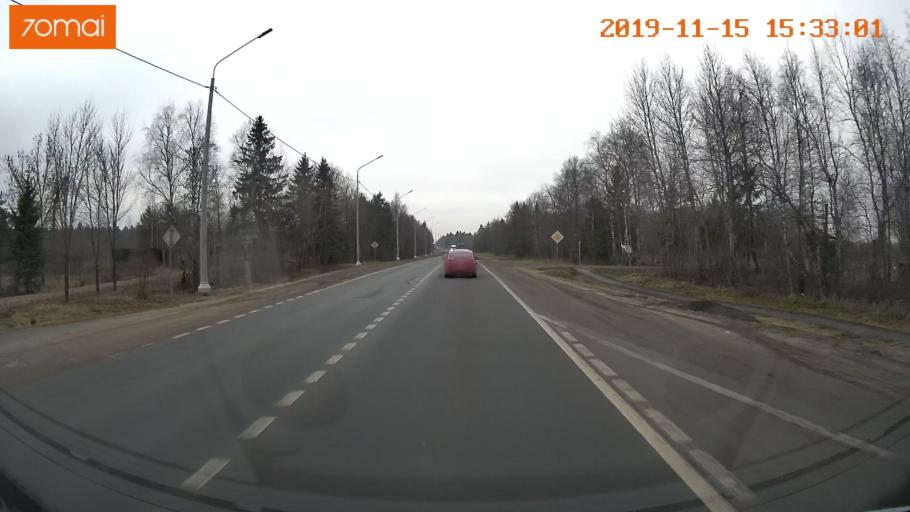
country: RU
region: Jaroslavl
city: Danilov
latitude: 58.0849
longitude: 40.0946
